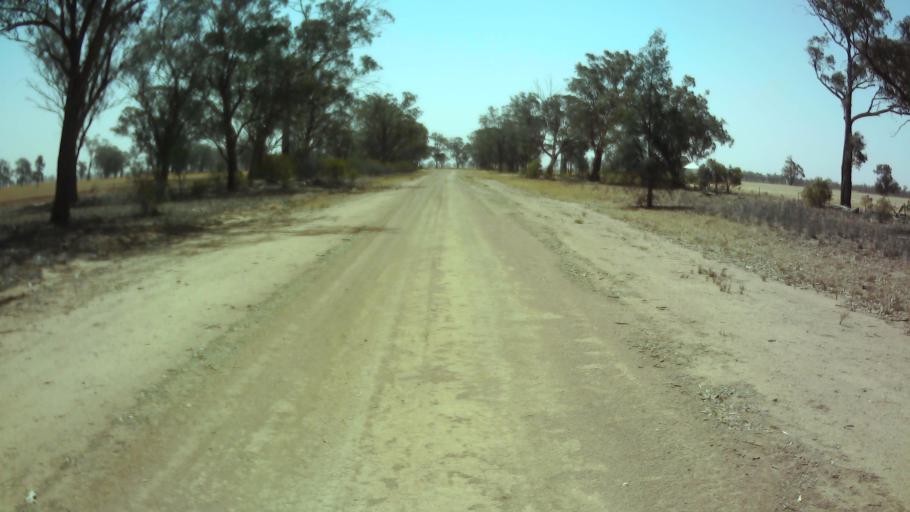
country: AU
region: New South Wales
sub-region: Weddin
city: Grenfell
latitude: -33.9385
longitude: 147.8090
